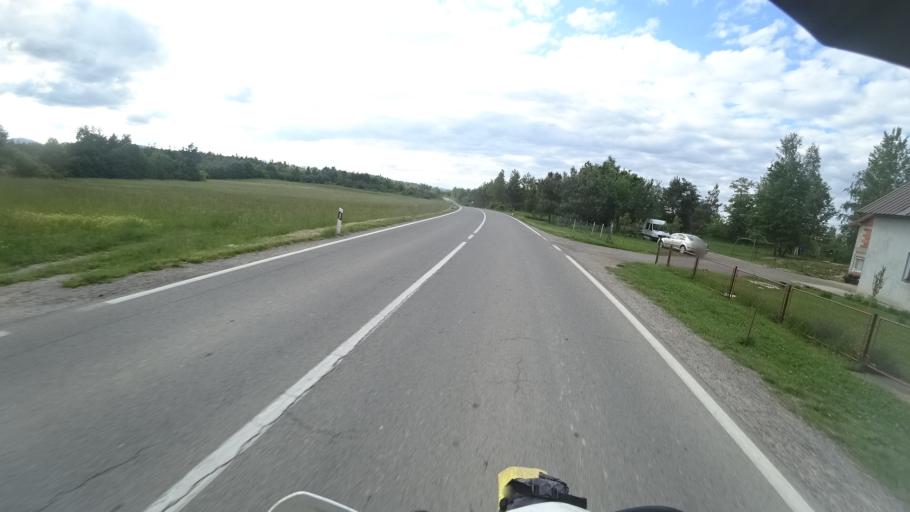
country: HR
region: Licko-Senjska
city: Gospic
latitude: 44.5223
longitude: 15.4144
